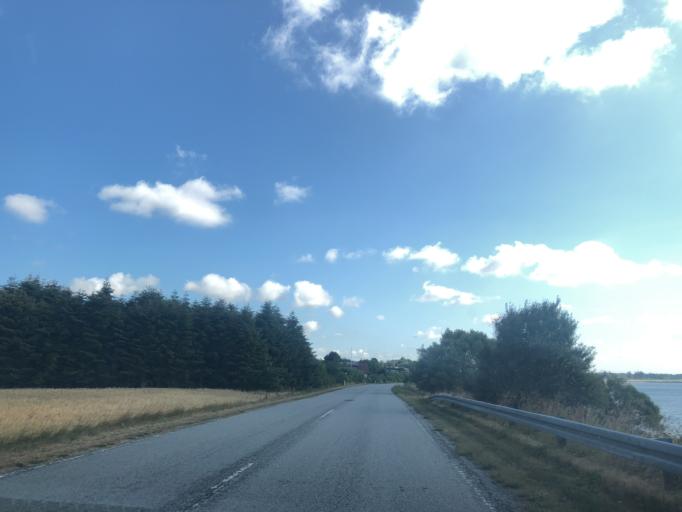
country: DK
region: North Denmark
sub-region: Morso Kommune
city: Nykobing Mors
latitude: 56.9999
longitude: 8.9239
